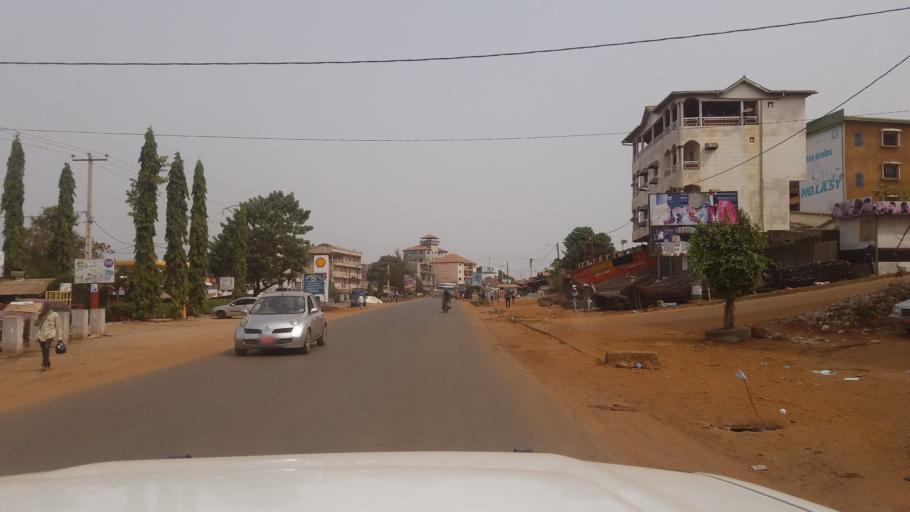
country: GN
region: Conakry
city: Conakry
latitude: 9.6502
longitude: -13.6024
